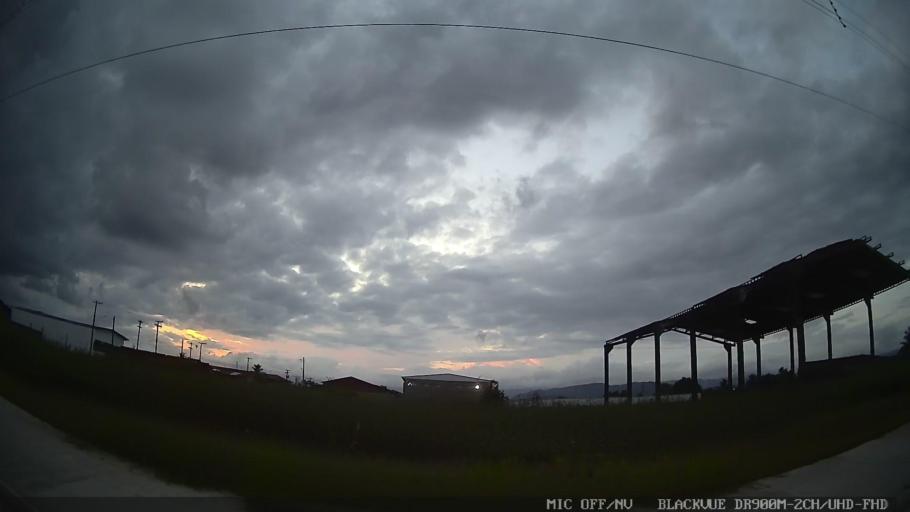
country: BR
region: Sao Paulo
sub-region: Itanhaem
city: Itanhaem
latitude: -24.1897
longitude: -46.8311
